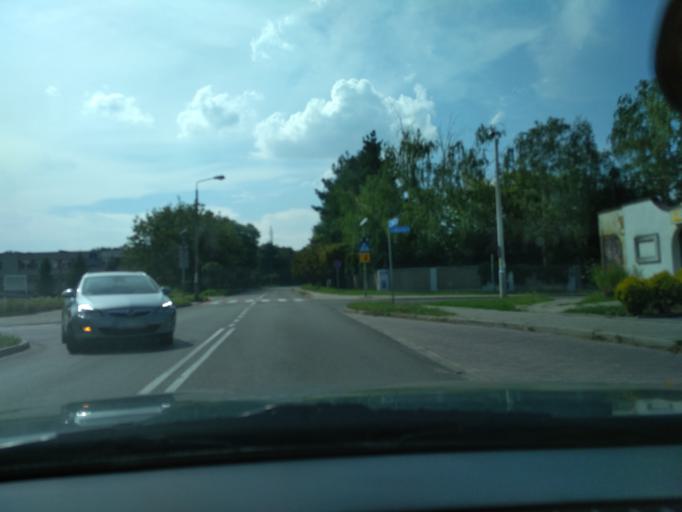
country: PL
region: Silesian Voivodeship
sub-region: Powiat raciborski
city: Raciborz
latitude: 50.0842
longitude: 18.1990
